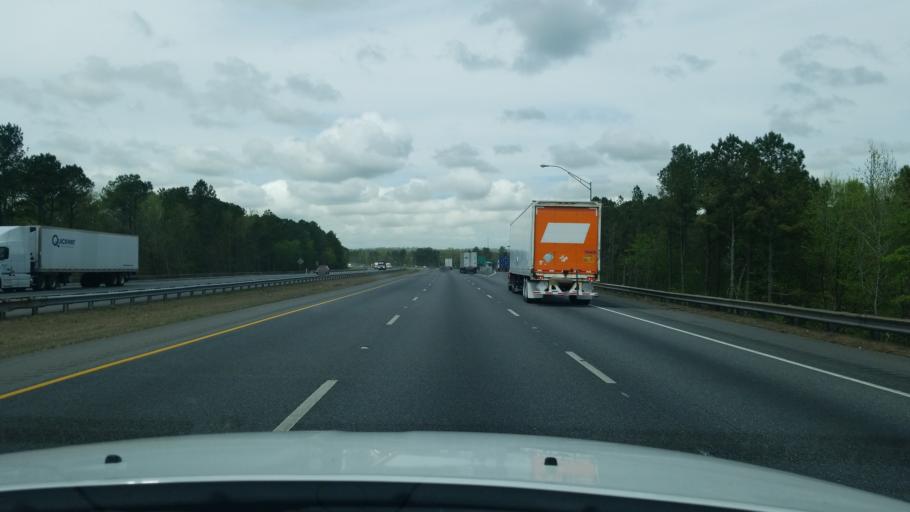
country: US
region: Georgia
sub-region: Whitfield County
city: Varnell
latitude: 34.8760
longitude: -85.0447
